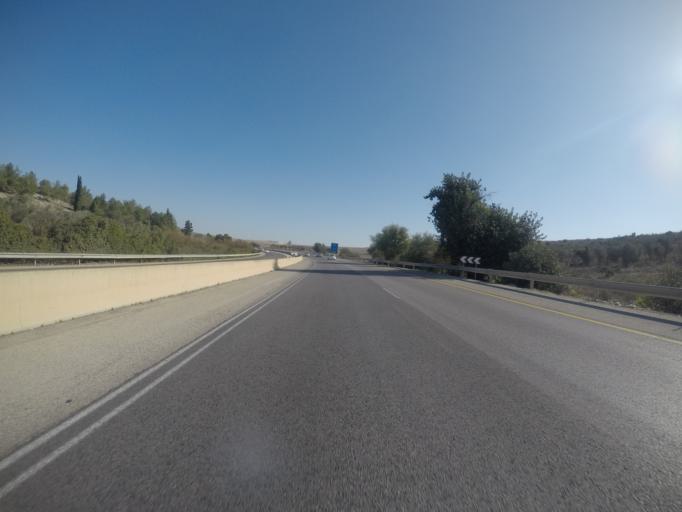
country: IL
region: Haifa
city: El Fureidis
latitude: 32.6045
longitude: 35.0275
